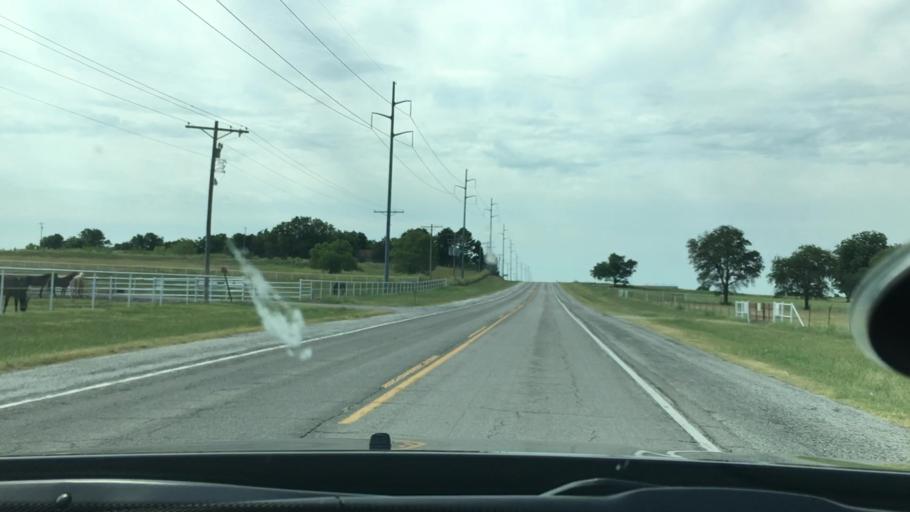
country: US
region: Oklahoma
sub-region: Carter County
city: Ardmore
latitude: 34.3288
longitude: -97.1430
